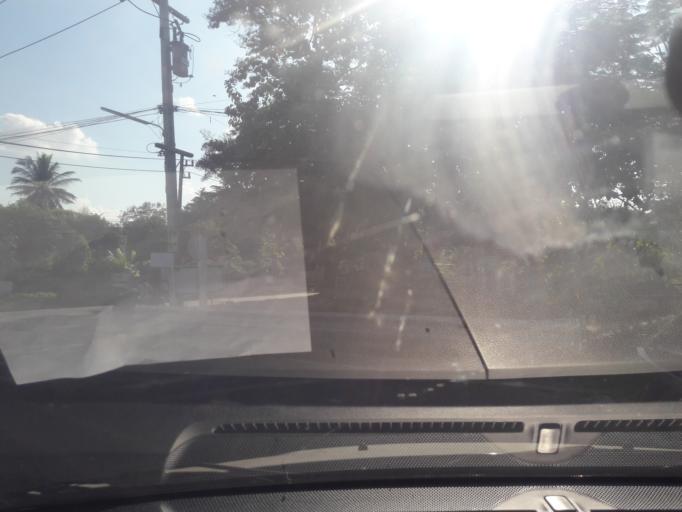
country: TH
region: Chiang Mai
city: San Kamphaeng
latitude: 18.7412
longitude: 99.1581
